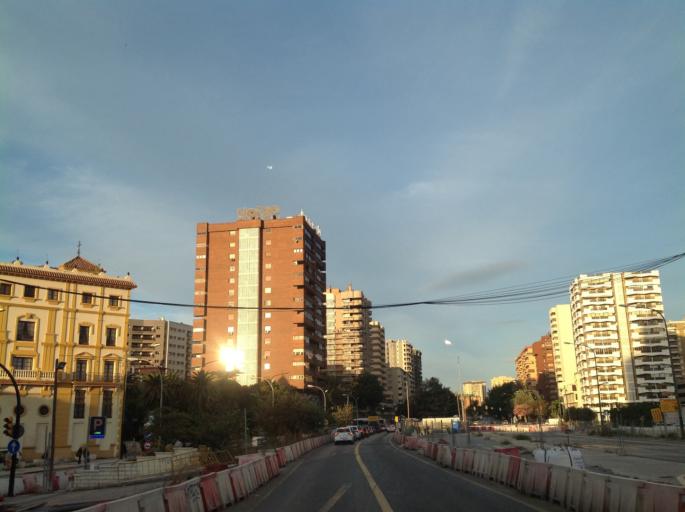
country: ES
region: Andalusia
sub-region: Provincia de Malaga
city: Malaga
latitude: 36.7167
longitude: -4.4273
